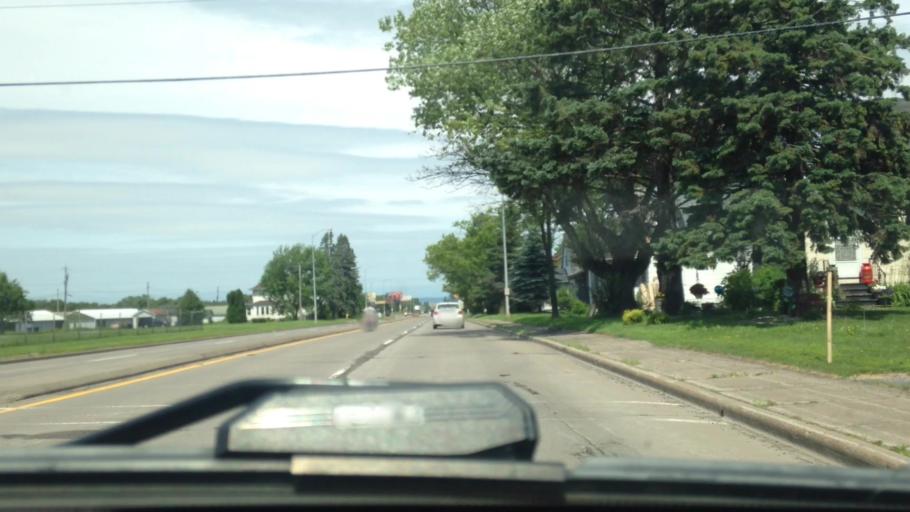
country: US
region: Wisconsin
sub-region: Douglas County
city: Superior
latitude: 46.6757
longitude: -92.0079
